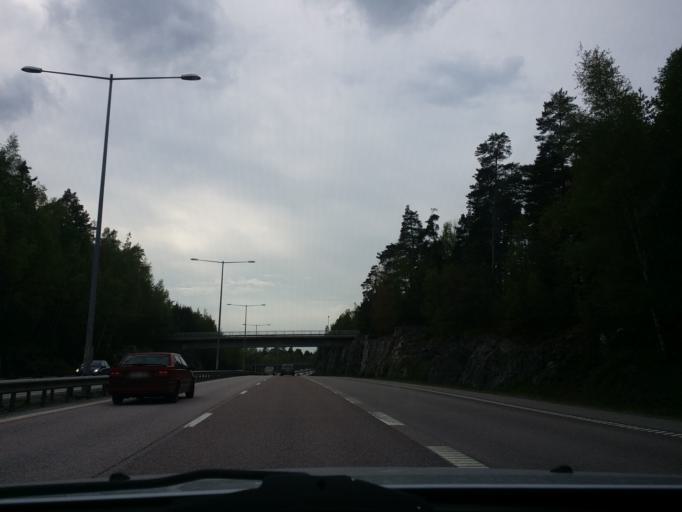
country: SE
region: Vaestmanland
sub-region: Vasteras
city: Vasteras
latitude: 59.6099
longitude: 16.5950
